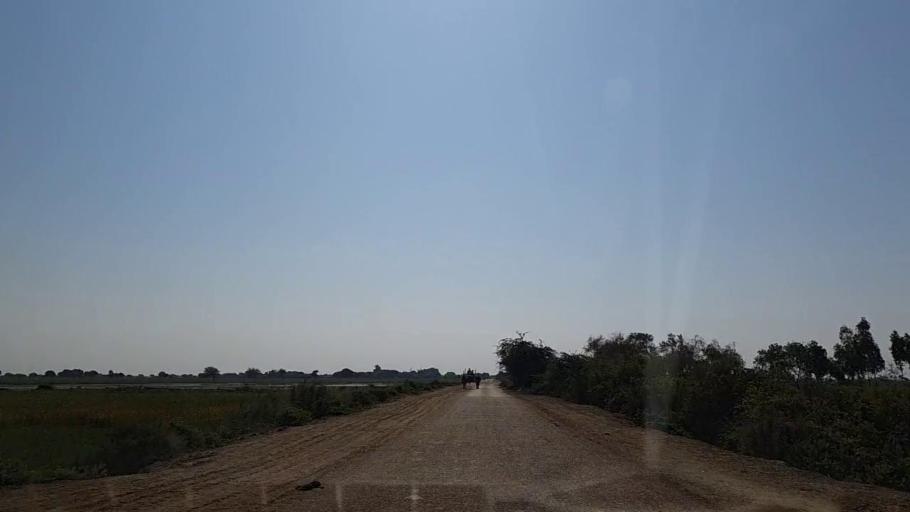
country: PK
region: Sindh
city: Chuhar Jamali
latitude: 24.5207
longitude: 68.0935
